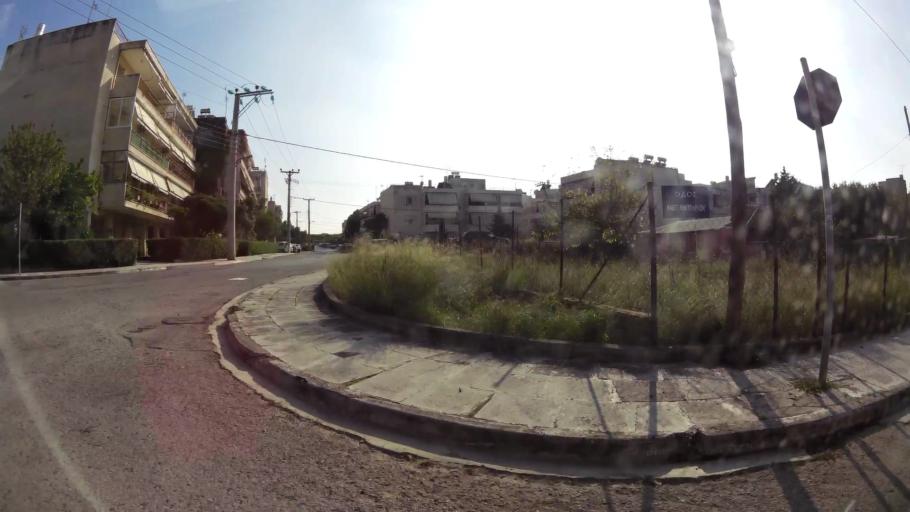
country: GR
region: Attica
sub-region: Nomarchia Anatolikis Attikis
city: Acharnes
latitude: 38.0820
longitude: 23.7186
